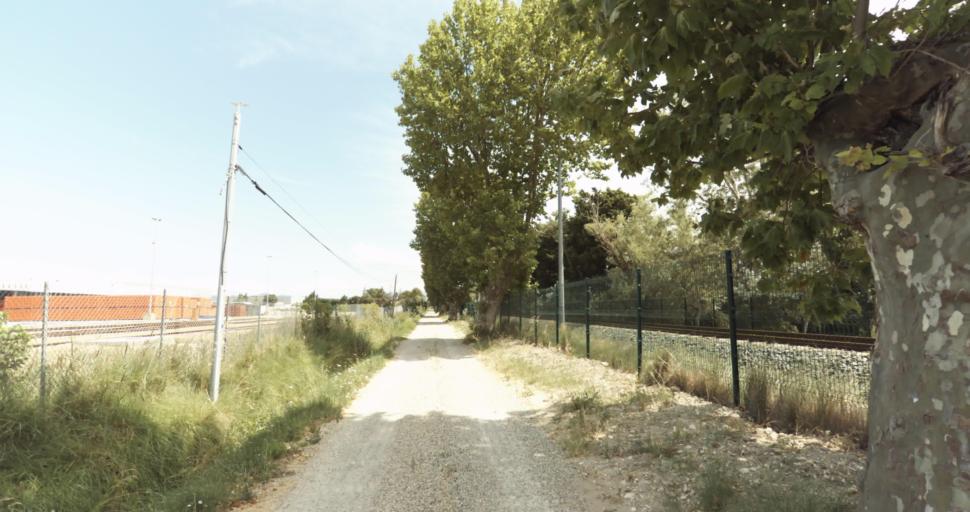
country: FR
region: Provence-Alpes-Cote d'Azur
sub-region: Departement du Vaucluse
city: Monteux
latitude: 44.0310
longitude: 4.9714
